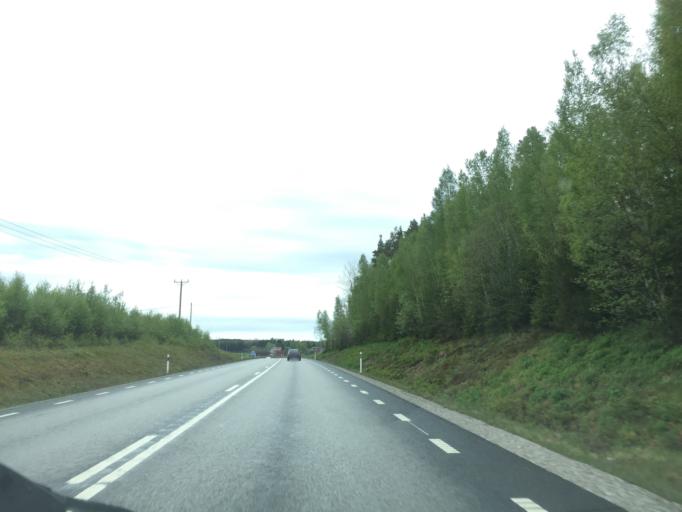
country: SE
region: OErebro
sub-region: Lindesbergs Kommun
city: Lindesberg
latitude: 59.5805
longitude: 15.2012
